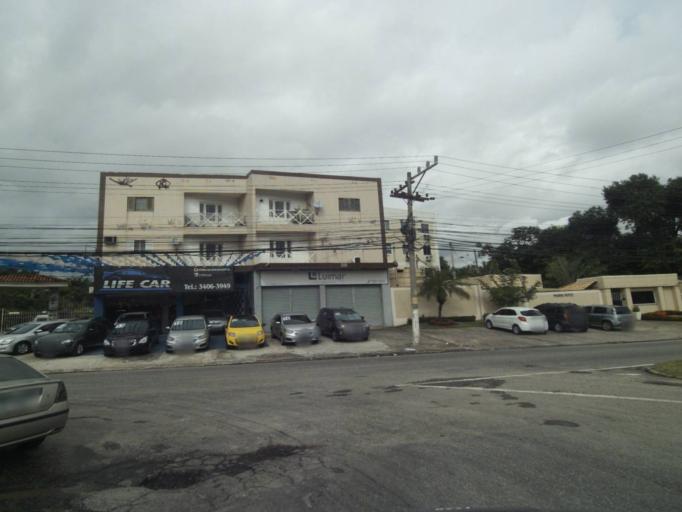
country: BR
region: Rio de Janeiro
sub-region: Nova Iguacu
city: Nova Iguacu
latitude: -22.8626
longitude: -43.5427
